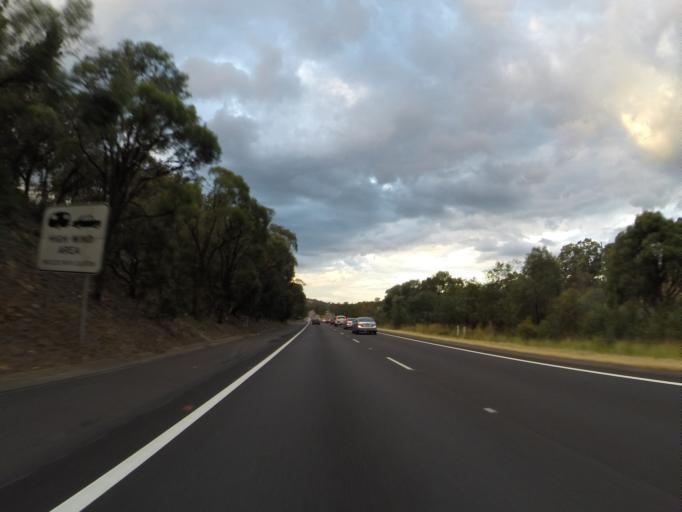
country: AU
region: New South Wales
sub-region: Wollondilly
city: Douglas Park
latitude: -34.1944
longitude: 150.7101
